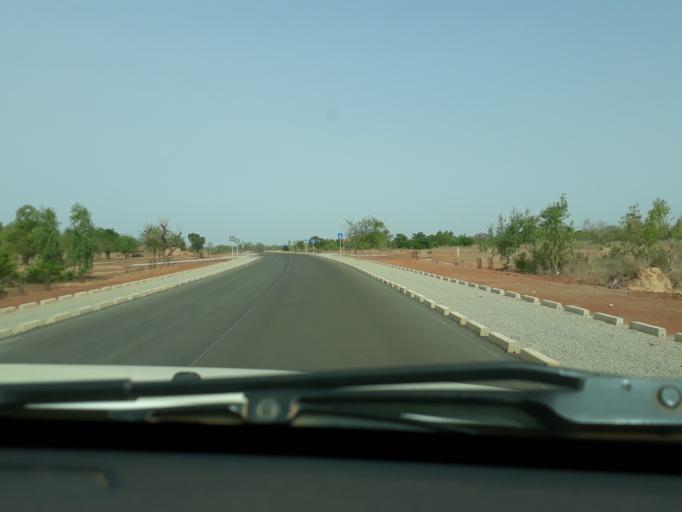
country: BF
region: Plateau-Central
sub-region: Province d'Oubritenga
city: Ziniare
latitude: 12.5502
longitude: -1.3952
